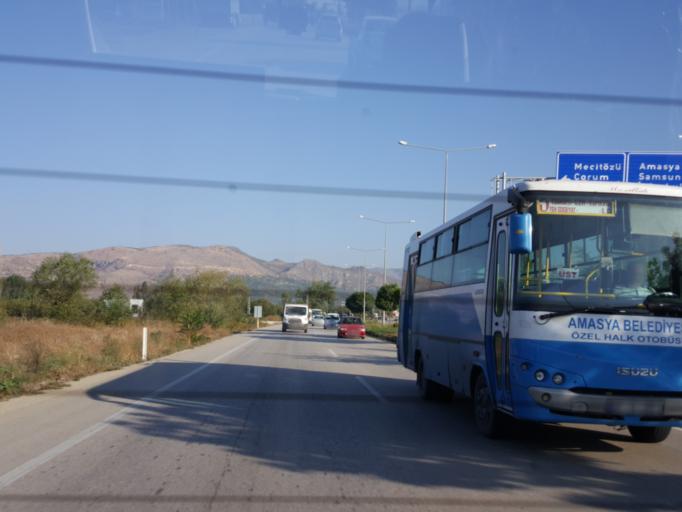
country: TR
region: Amasya
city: Amasya
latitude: 40.5665
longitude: 35.7878
